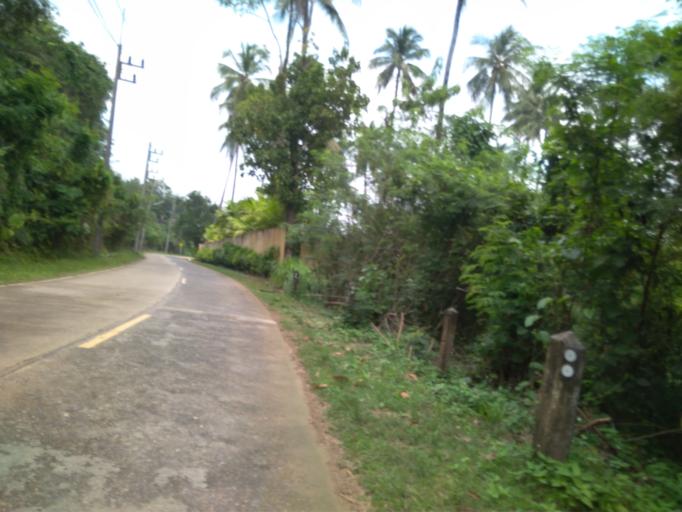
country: TH
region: Phangnga
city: Ko Yao
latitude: 8.1139
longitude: 98.6235
